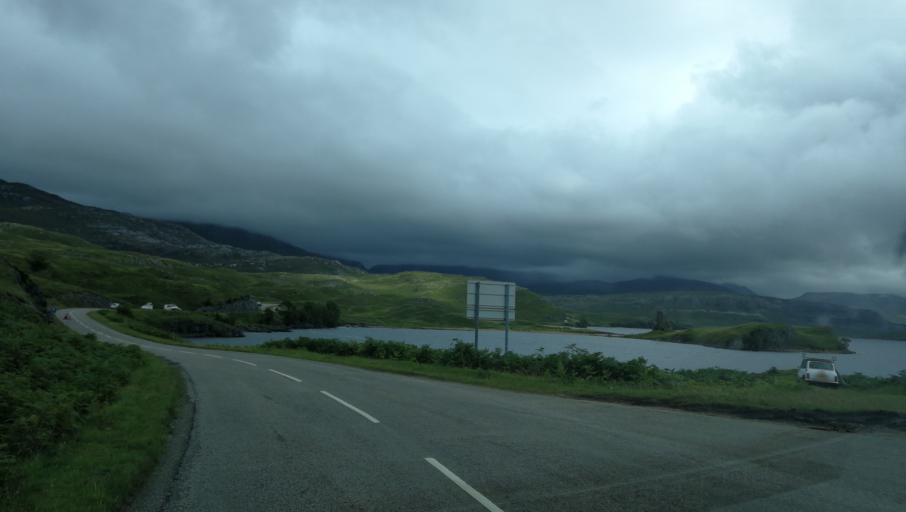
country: GB
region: Scotland
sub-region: Highland
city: Ullapool
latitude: 58.1699
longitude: -4.9982
